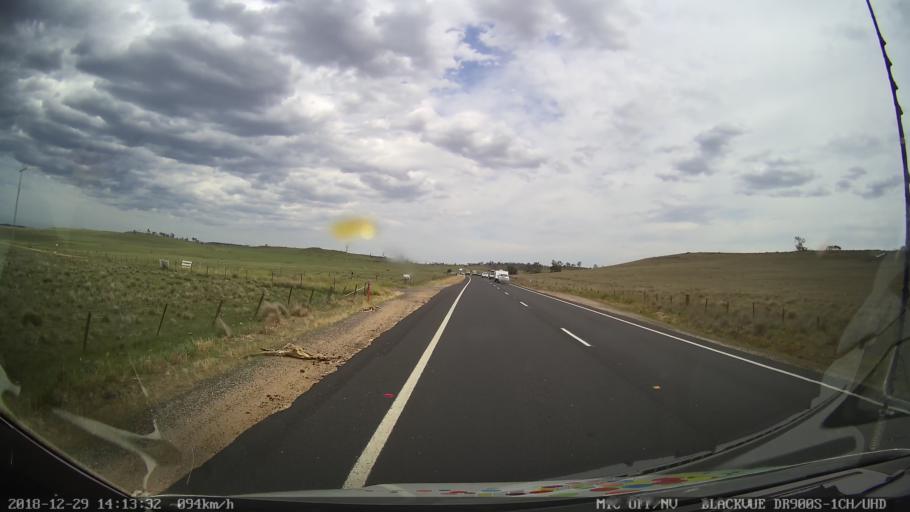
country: AU
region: New South Wales
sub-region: Cooma-Monaro
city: Cooma
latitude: -36.4295
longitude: 149.2384
